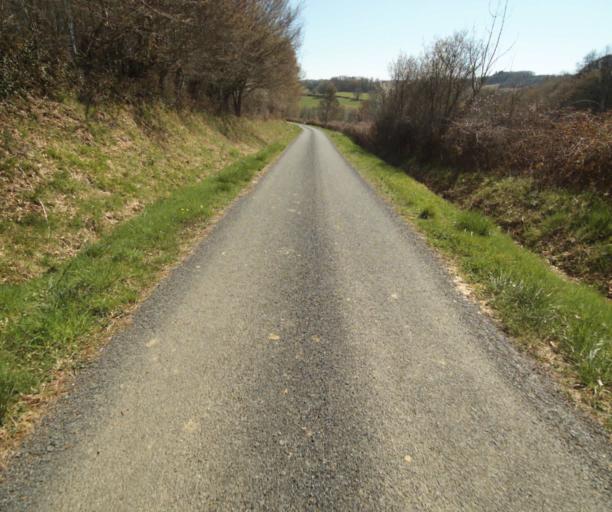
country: FR
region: Limousin
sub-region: Departement de la Correze
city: Chamboulive
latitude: 45.4603
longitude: 1.6725
